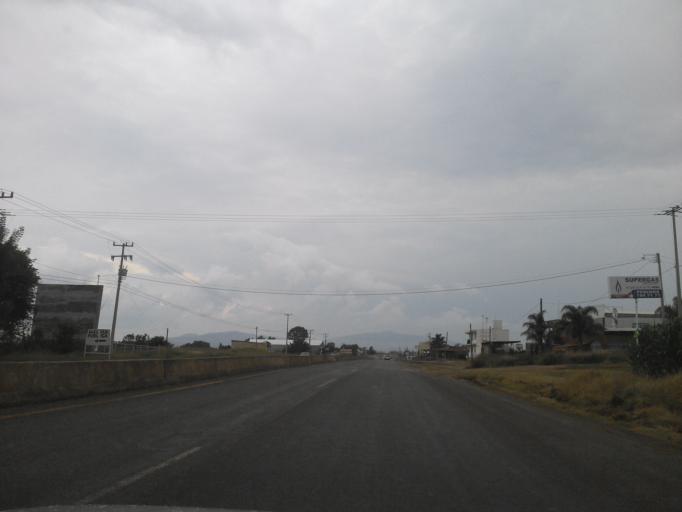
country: MX
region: Jalisco
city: Arandas
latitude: 20.7197
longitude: -102.4462
